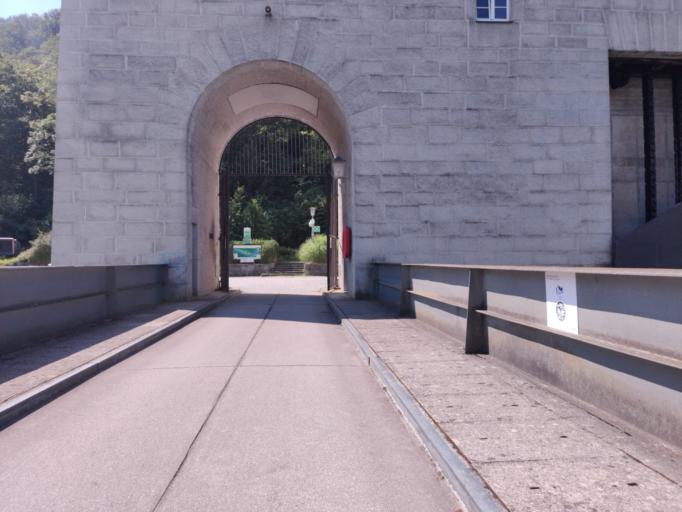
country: DE
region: Bavaria
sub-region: Lower Bavaria
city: Untergriesbach
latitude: 48.5164
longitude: 13.7063
